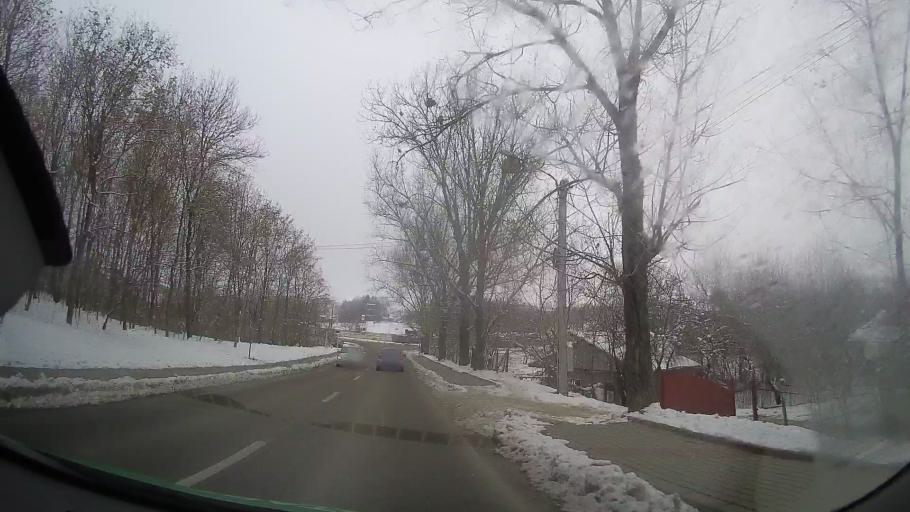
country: RO
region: Vaslui
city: Vaslui
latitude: 46.6453
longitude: 27.7205
